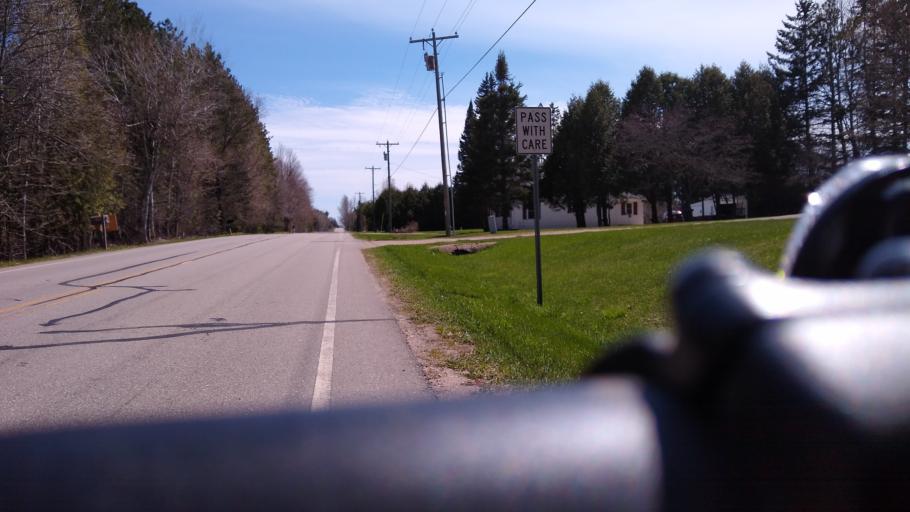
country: US
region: Michigan
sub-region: Delta County
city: Escanaba
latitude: 45.7285
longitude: -87.2025
